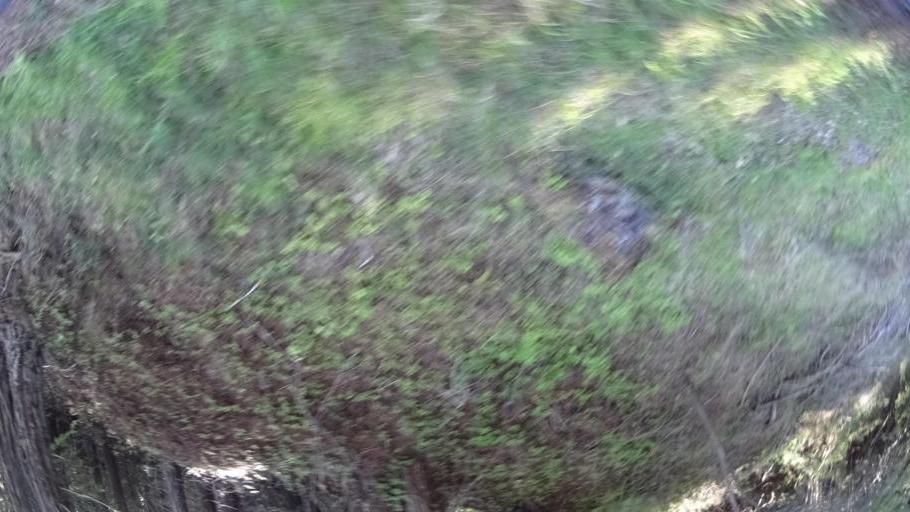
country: US
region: California
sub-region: Humboldt County
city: Rio Dell
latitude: 40.4533
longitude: -123.9877
